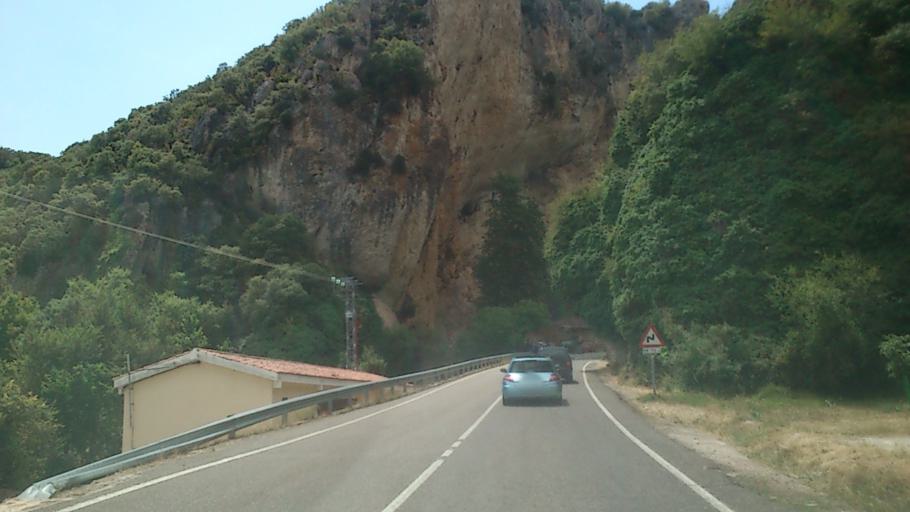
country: ES
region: Castille and Leon
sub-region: Provincia de Burgos
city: Frias
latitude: 42.7493
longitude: -3.3063
